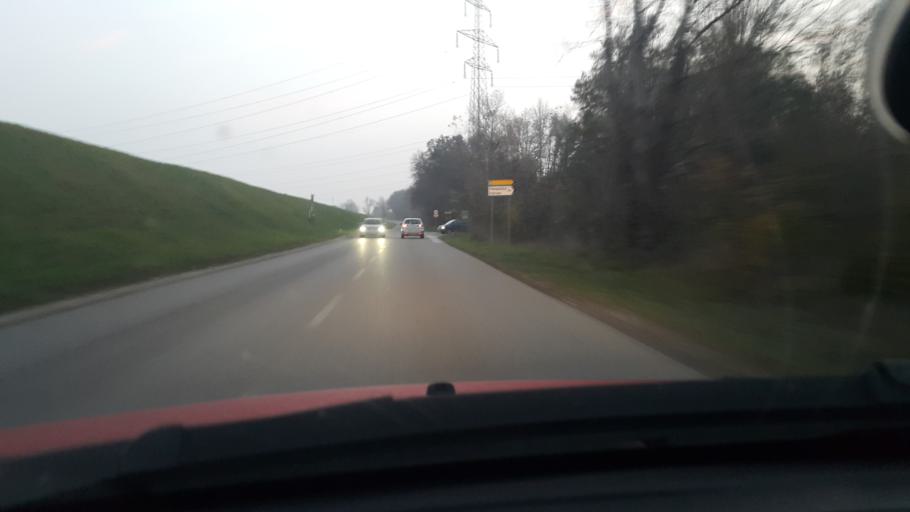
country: SI
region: Miklavz na Dravskem Polju
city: Miklavz na Dravskem Polju
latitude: 46.5211
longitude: 15.7005
